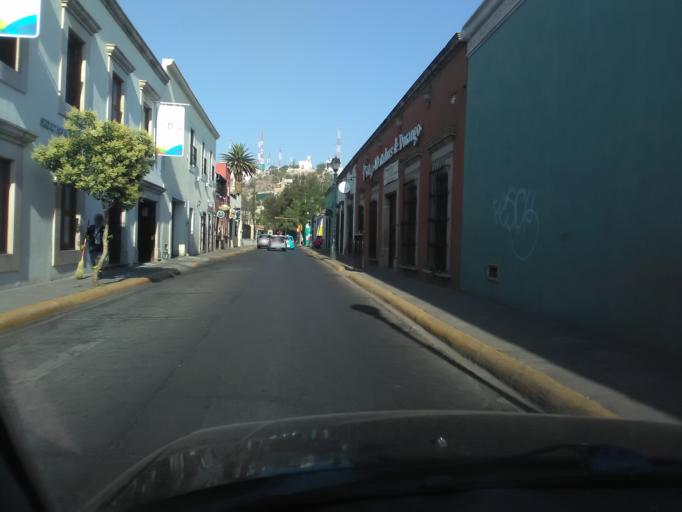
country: MX
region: Durango
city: Victoria de Durango
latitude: 24.0225
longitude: -104.6758
